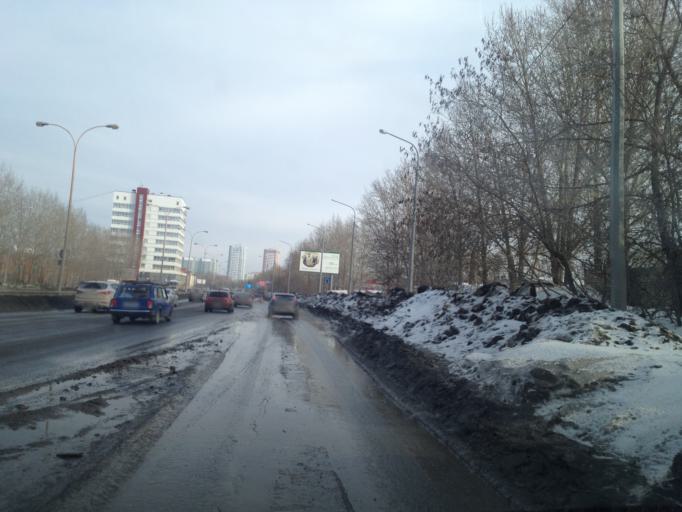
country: RU
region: Sverdlovsk
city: Yekaterinburg
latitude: 56.7881
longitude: 60.6197
